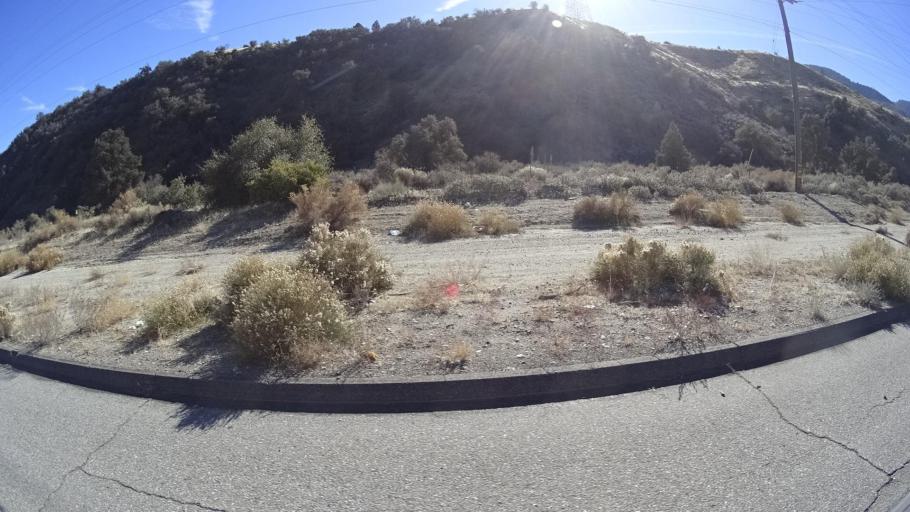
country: US
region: California
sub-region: Kern County
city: Frazier Park
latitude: 34.8181
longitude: -118.9063
